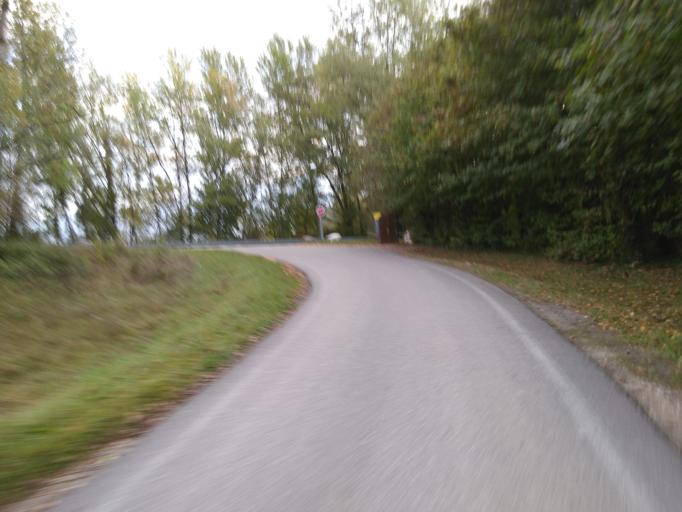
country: FR
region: Rhone-Alpes
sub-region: Departement de l'Isere
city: Corenc
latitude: 45.2020
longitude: 5.7700
